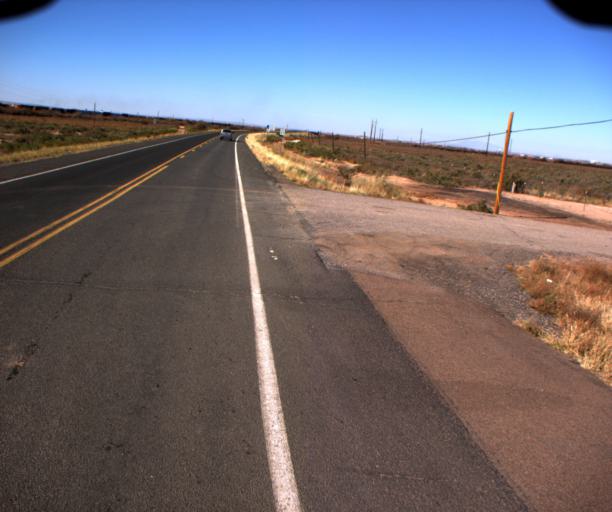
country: US
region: Arizona
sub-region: Navajo County
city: Winslow
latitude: 35.0057
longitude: -110.6439
